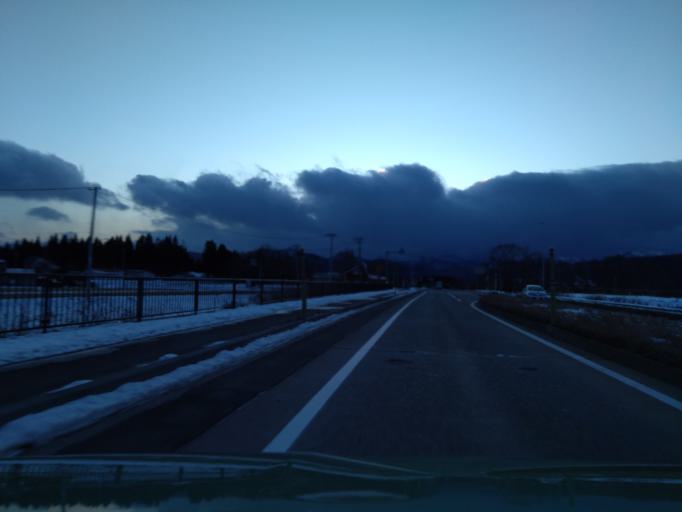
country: JP
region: Iwate
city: Shizukuishi
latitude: 39.7006
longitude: 140.9591
